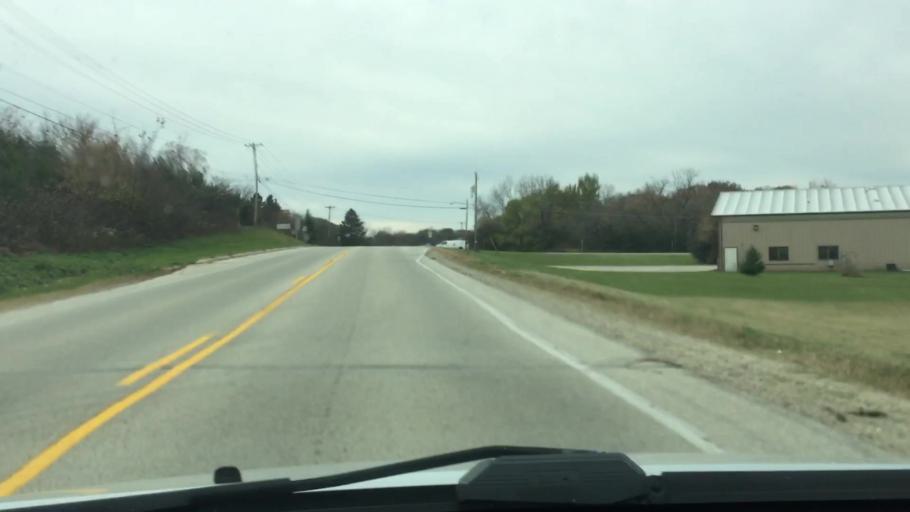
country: US
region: Wisconsin
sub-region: Waukesha County
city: Mukwonago
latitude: 42.8936
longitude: -88.2760
